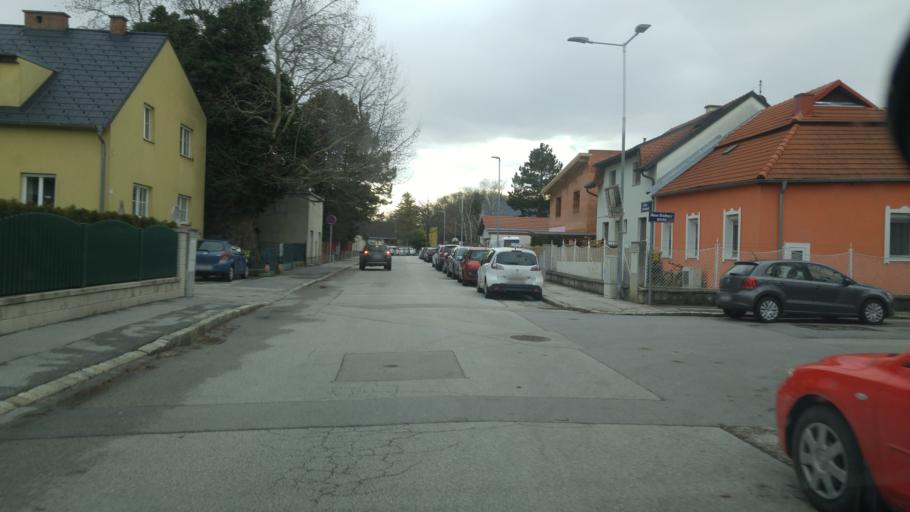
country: AT
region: Lower Austria
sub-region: Politischer Bezirk Wien-Umgebung
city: Himberg
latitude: 48.0834
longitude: 16.4365
